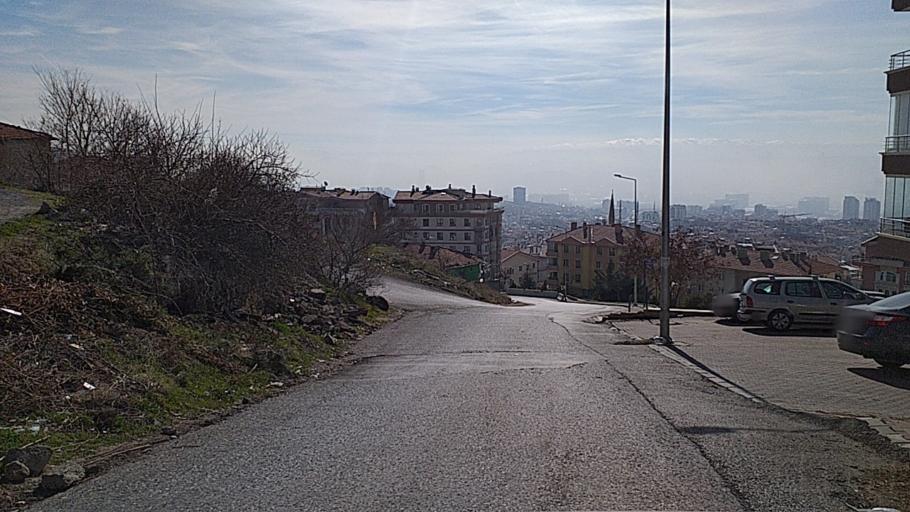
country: TR
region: Ankara
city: Ankara
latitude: 39.9899
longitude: 32.8130
